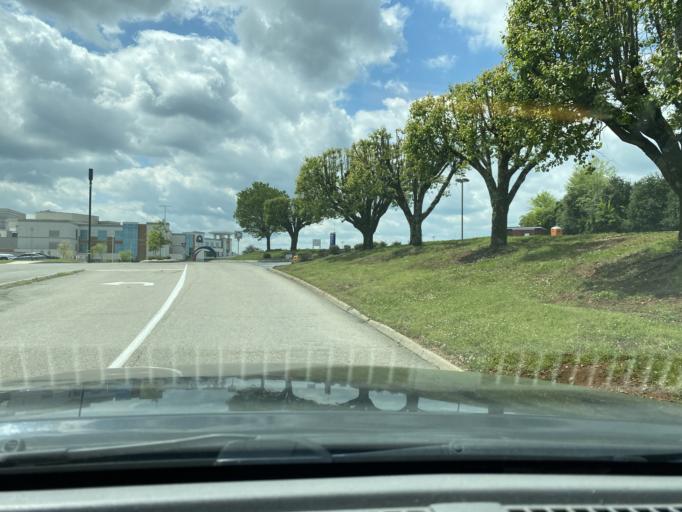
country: US
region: Tennessee
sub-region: Knox County
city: Farragut
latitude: 35.9184
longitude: -84.0985
